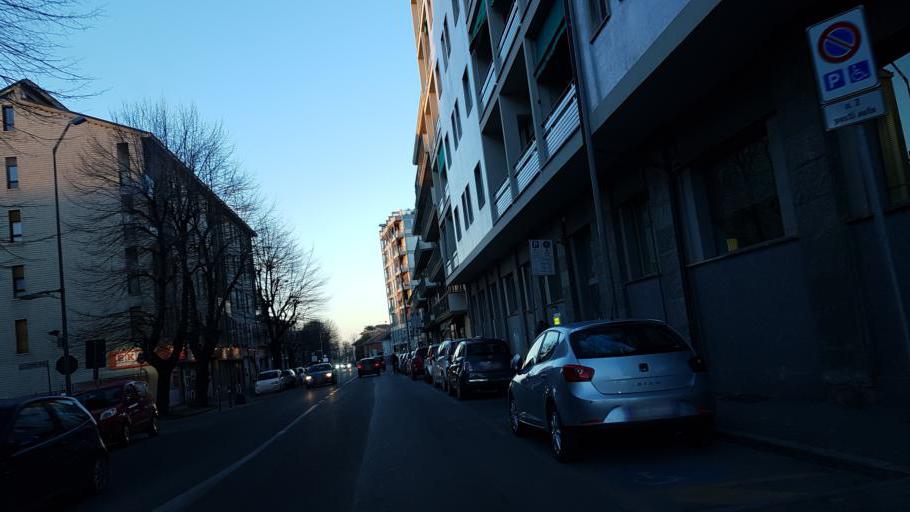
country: IT
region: Piedmont
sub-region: Provincia di Alessandria
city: Tortona
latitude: 44.8952
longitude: 8.8622
